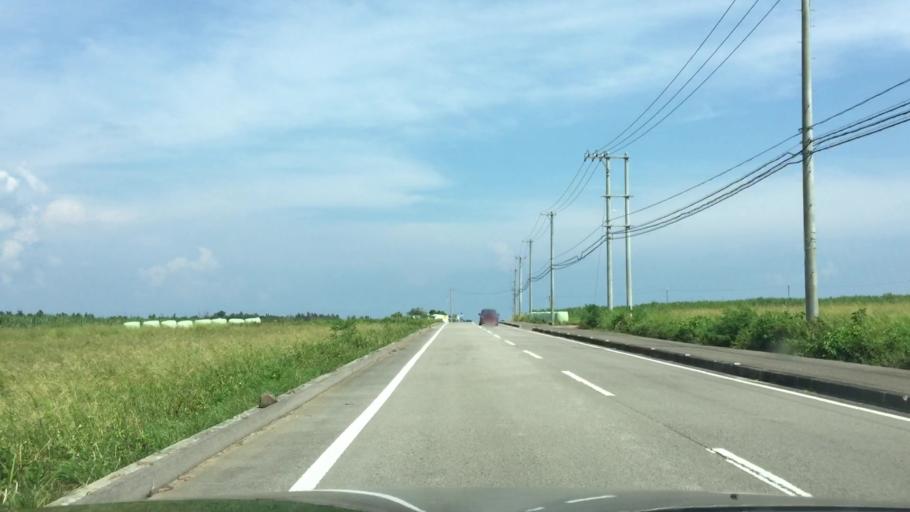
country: JP
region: Okinawa
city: Ishigaki
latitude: 24.5061
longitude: 124.2720
